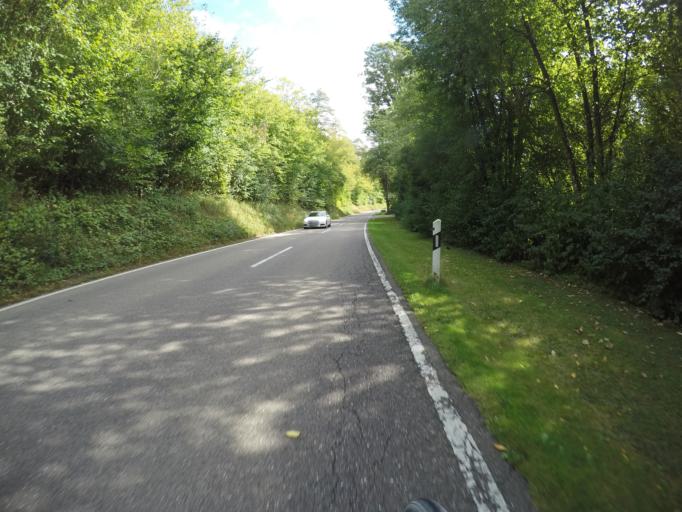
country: DE
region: Baden-Wuerttemberg
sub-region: Regierungsbezirk Stuttgart
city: Weissach
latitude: 48.8511
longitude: 8.9603
